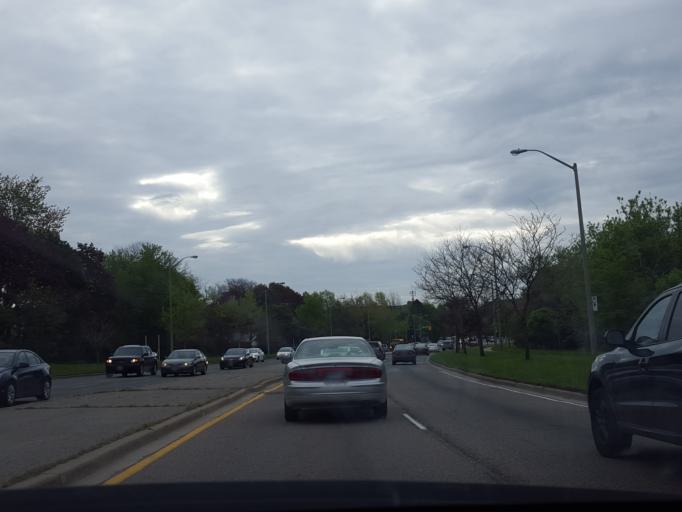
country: CA
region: Ontario
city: Willowdale
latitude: 43.7948
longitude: -79.3400
